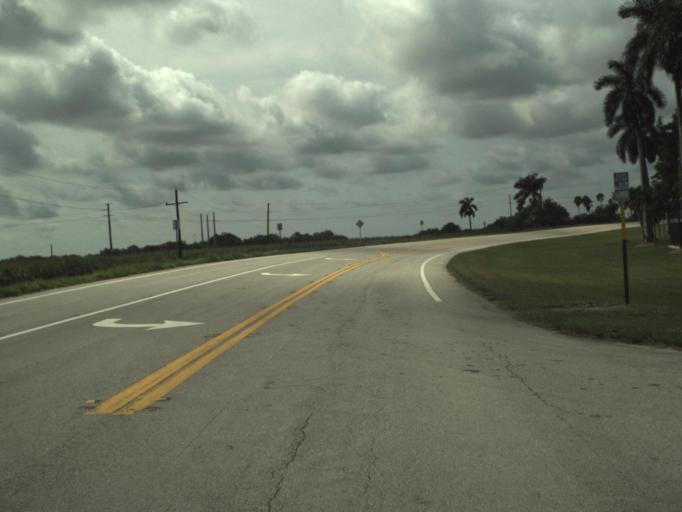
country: US
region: Florida
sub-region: Palm Beach County
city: Belle Glade
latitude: 26.7507
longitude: -80.6822
